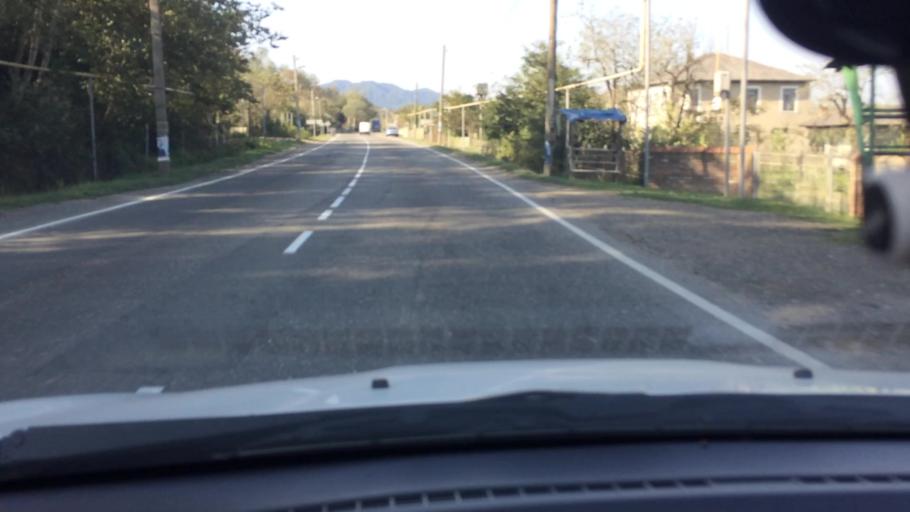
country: GE
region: Guria
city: Lanchkhuti
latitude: 42.0856
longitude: 42.1177
